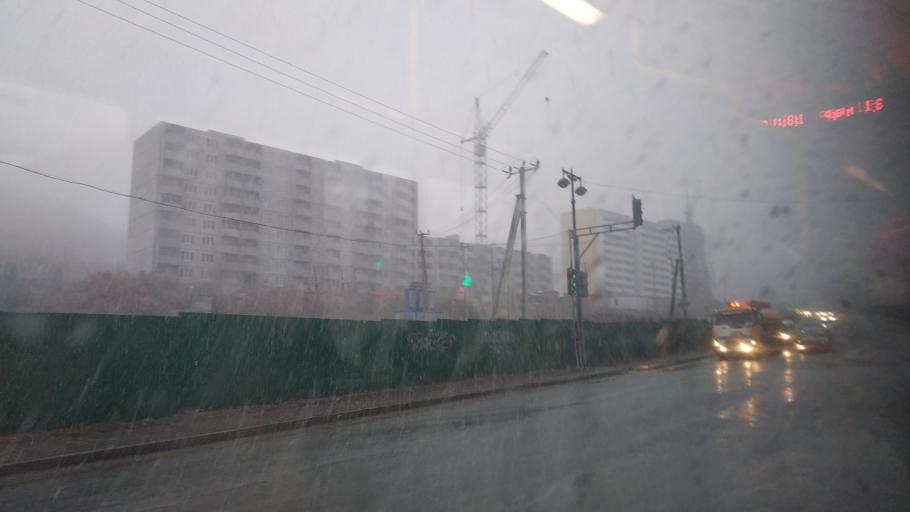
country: RU
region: Primorskiy
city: Vladivostok
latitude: 43.1673
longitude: 131.9577
